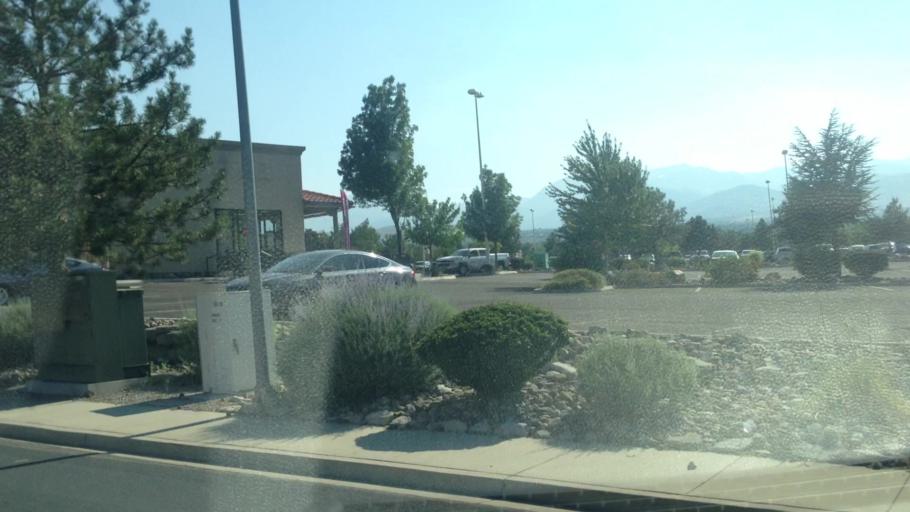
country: US
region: Nevada
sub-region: Washoe County
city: Sparks
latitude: 39.4225
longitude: -119.7542
